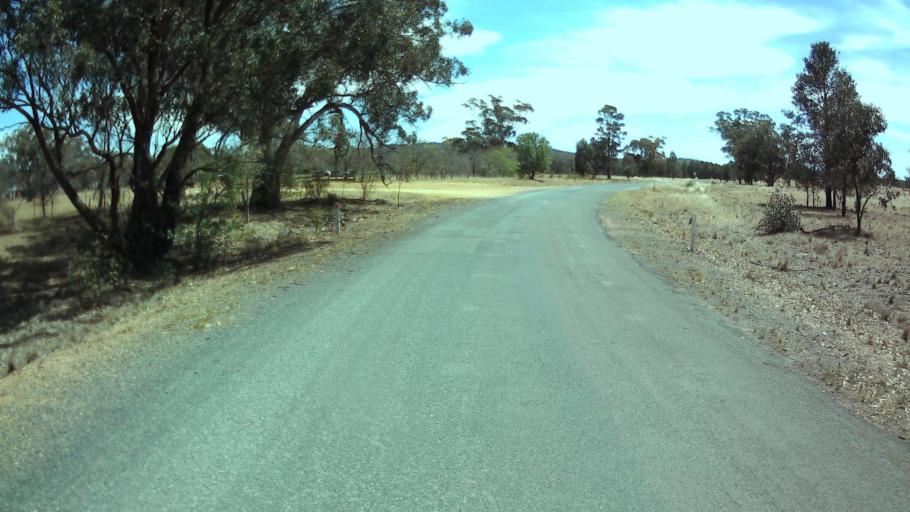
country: AU
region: New South Wales
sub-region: Weddin
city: Grenfell
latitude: -33.7758
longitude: 148.2076
